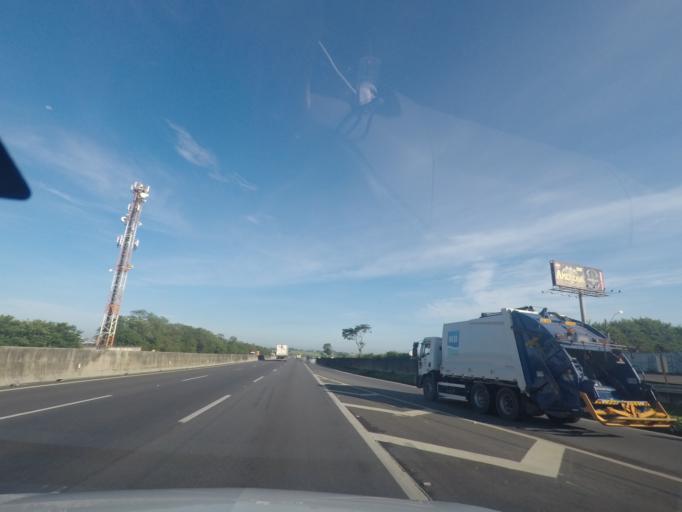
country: BR
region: Sao Paulo
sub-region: Nova Odessa
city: Nova Odessa
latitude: -22.7500
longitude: -47.2617
